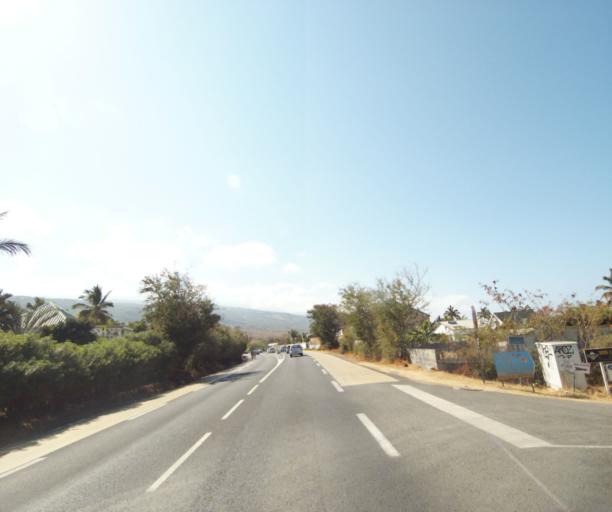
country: RE
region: Reunion
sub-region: Reunion
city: Trois-Bassins
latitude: -21.1056
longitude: 55.2502
